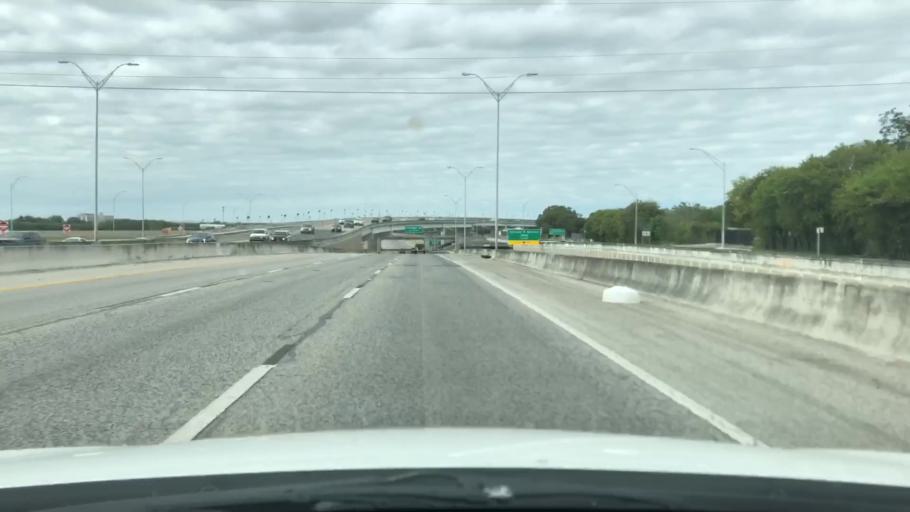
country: US
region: Texas
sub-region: Bexar County
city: Lackland Air Force Base
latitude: 29.4075
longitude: -98.5840
